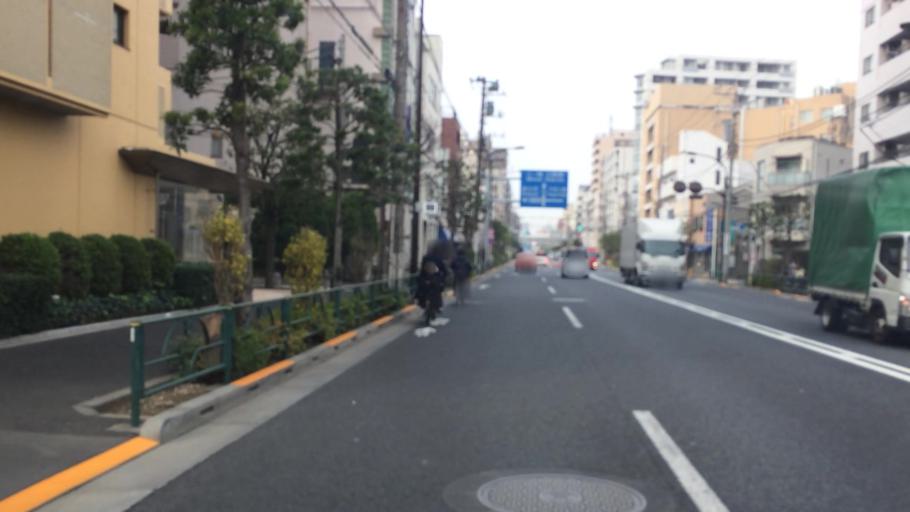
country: JP
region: Tokyo
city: Urayasu
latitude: 35.7163
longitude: 139.8242
